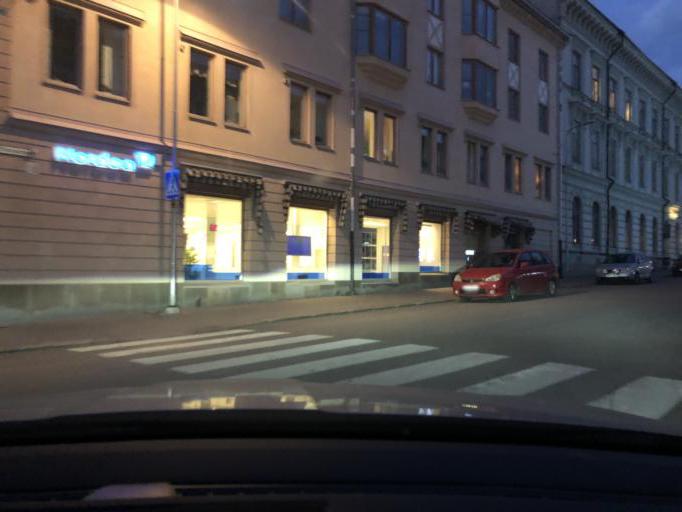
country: SE
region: Gaevleborg
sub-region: Hudiksvalls Kommun
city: Hudiksvall
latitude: 61.7276
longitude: 17.1084
